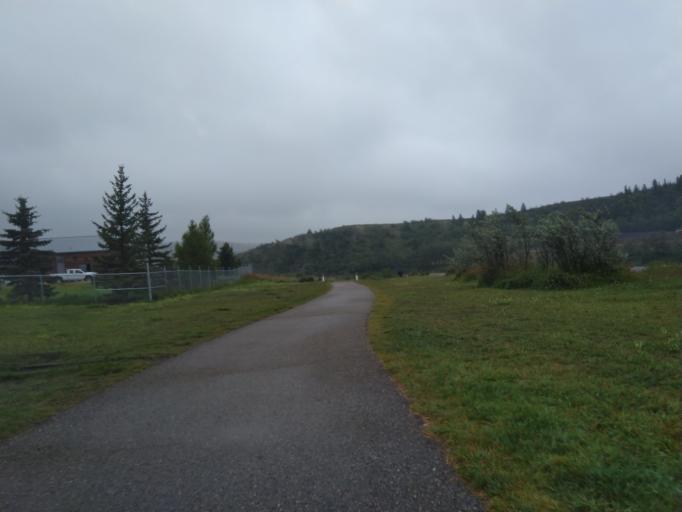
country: CA
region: Alberta
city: Cochrane
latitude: 51.1739
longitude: -114.4519
